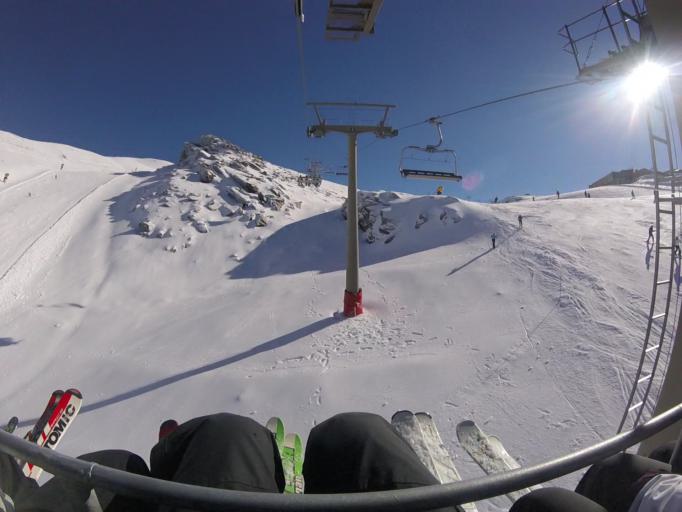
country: ES
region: Andalusia
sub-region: Provincia de Granada
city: Guejar-Sierra
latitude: 37.0753
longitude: -3.3873
